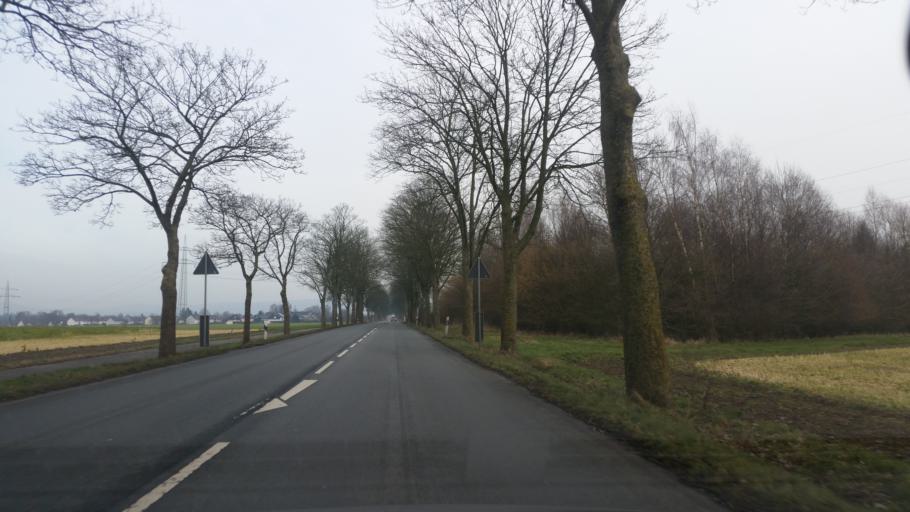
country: DE
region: North Rhine-Westphalia
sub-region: Regierungsbezirk Detmold
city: Lage
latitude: 52.0057
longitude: 8.8364
